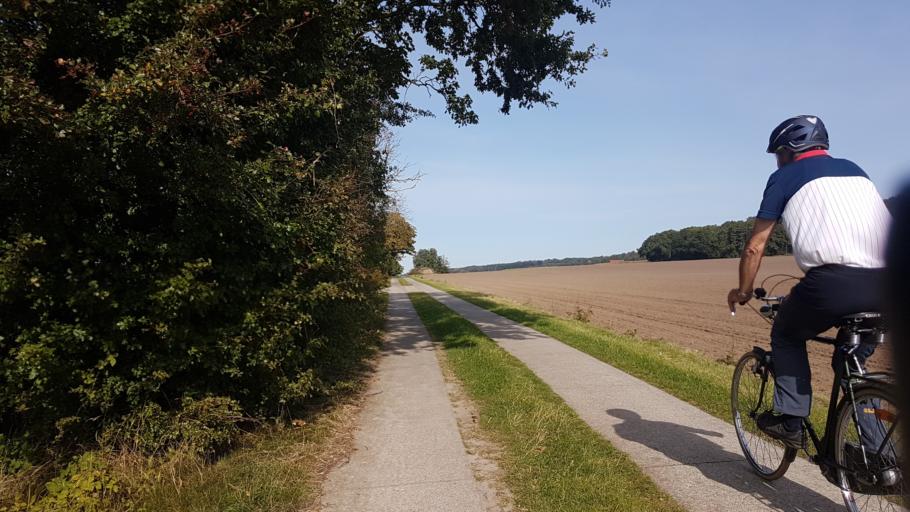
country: DE
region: Mecklenburg-Vorpommern
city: Gingst
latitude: 54.4103
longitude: 13.2570
